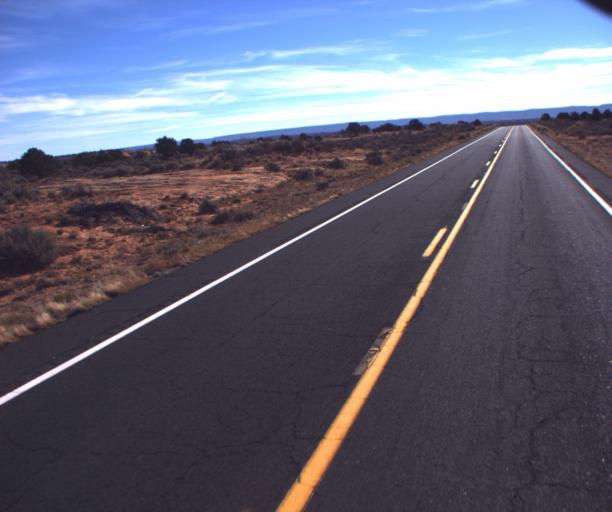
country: US
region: Arizona
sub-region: Coconino County
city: Kaibito
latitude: 36.5679
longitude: -110.7610
